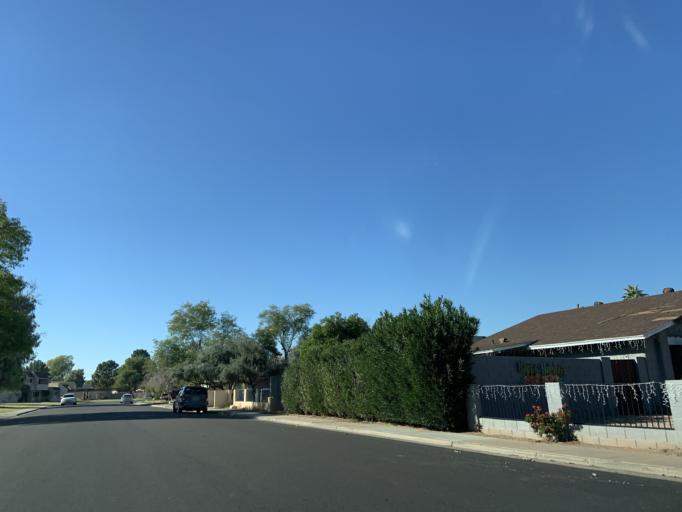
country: US
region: Arizona
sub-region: Maricopa County
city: Tempe
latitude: 33.3960
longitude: -111.8783
